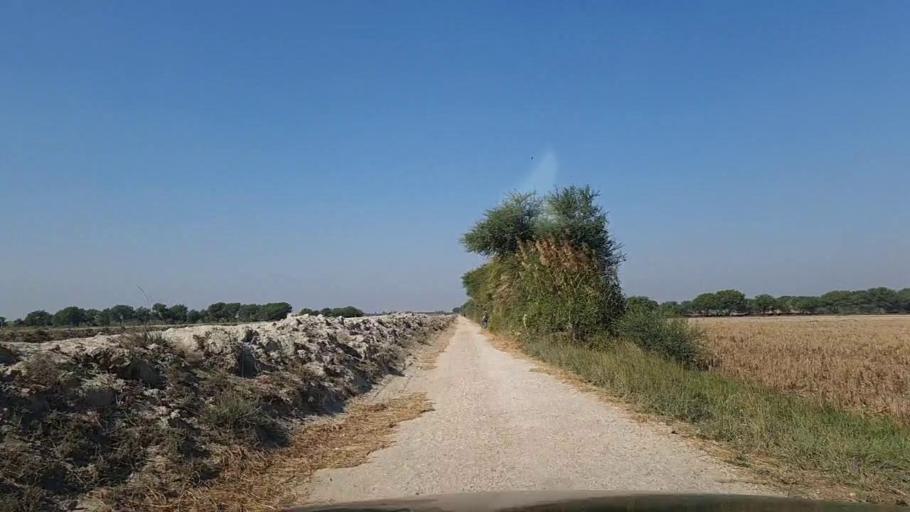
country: PK
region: Sindh
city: Mirpur Batoro
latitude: 24.7159
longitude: 68.2374
